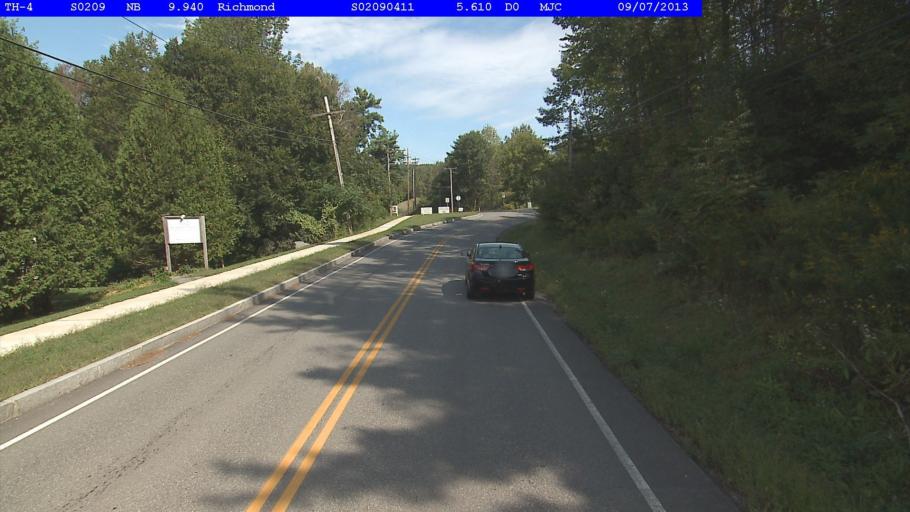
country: US
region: Vermont
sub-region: Chittenden County
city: Williston
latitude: 44.4108
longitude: -72.9917
